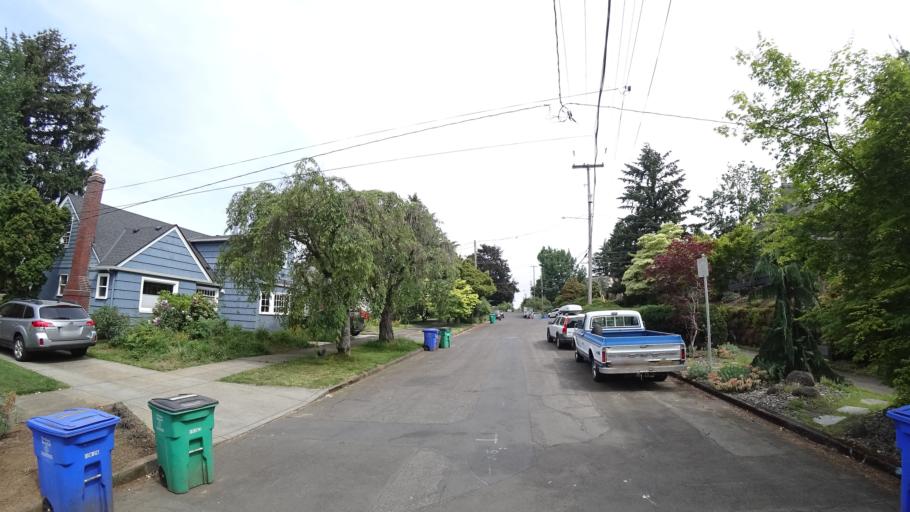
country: US
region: Oregon
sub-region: Multnomah County
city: Portland
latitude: 45.5309
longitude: -122.6127
